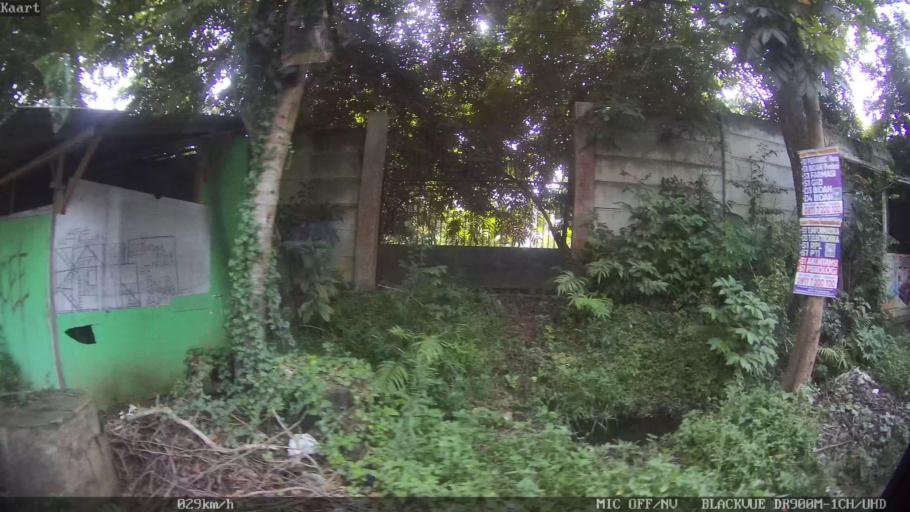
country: ID
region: Lampung
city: Bandarlampung
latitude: -5.4293
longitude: 105.2460
